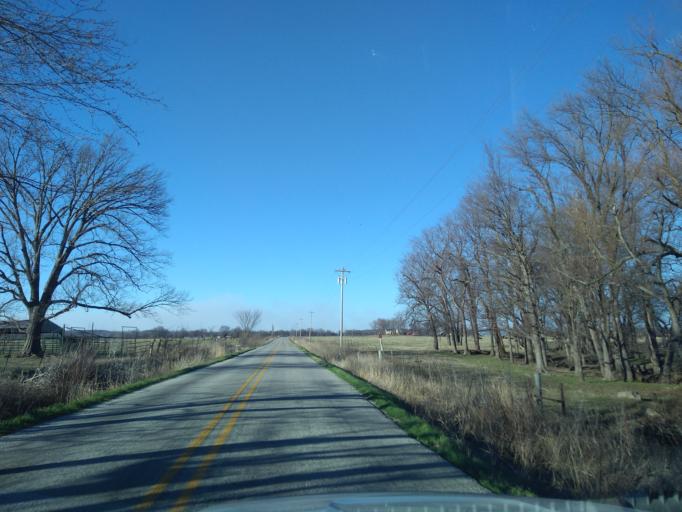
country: US
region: Arkansas
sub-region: Washington County
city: Lincoln
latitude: 36.0086
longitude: -94.3926
